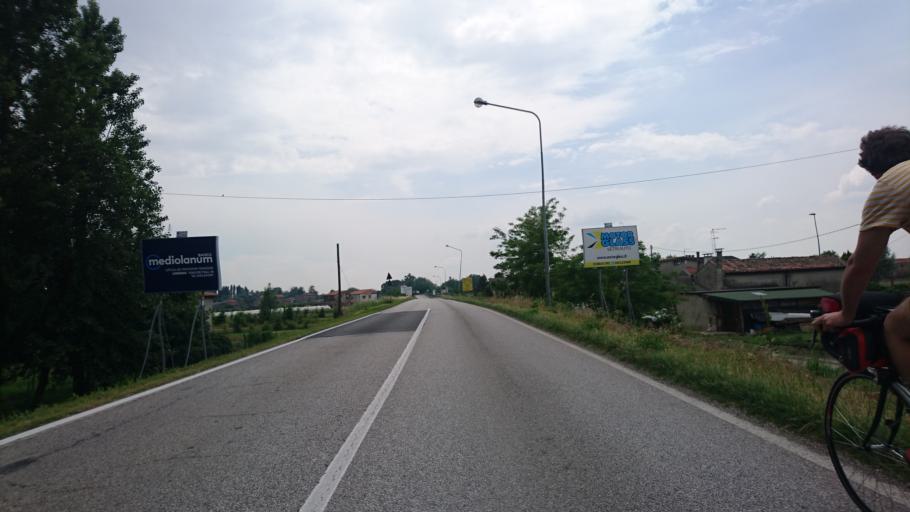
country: IT
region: Veneto
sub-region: Provincia di Rovigo
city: Badia Polesine
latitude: 45.0863
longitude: 11.4713
